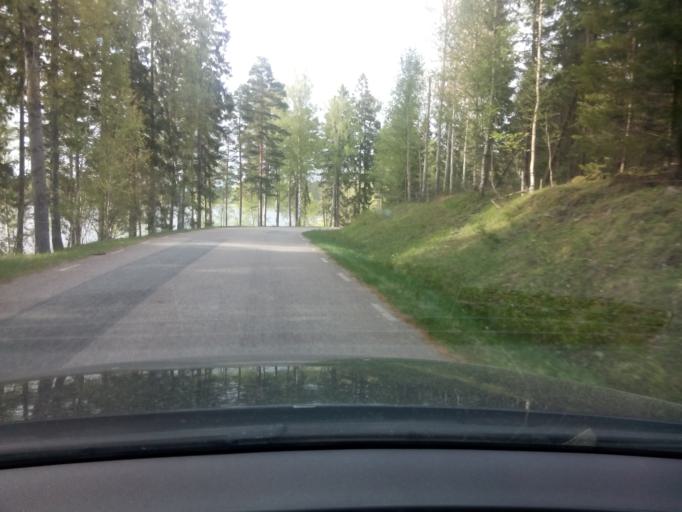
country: SE
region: Soedermanland
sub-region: Nykopings Kommun
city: Stigtomta
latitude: 58.9336
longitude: 16.8888
